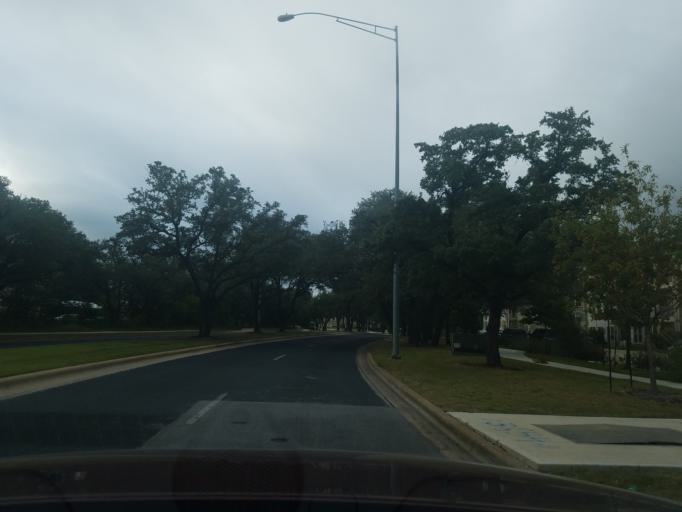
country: US
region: Texas
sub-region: Williamson County
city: Anderson Mill
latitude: 30.4732
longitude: -97.8106
